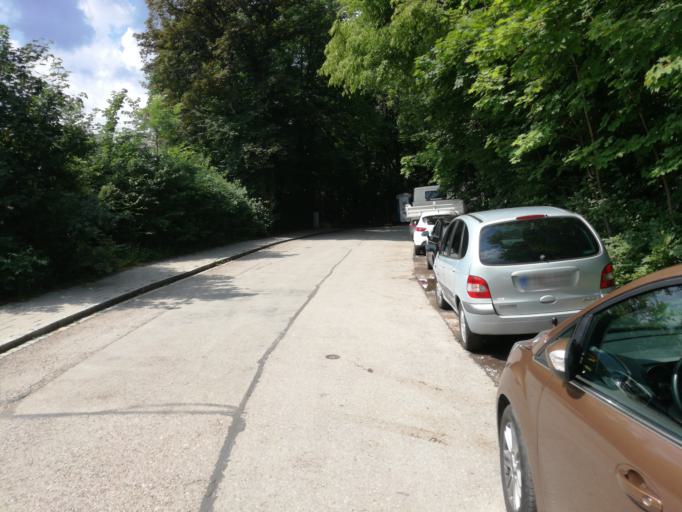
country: DE
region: Bavaria
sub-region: Upper Bavaria
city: Planegg
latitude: 48.1087
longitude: 11.4165
